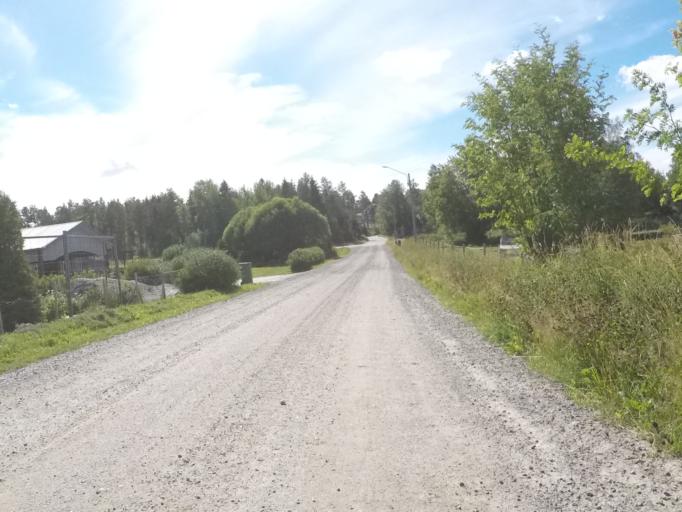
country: SE
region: Vaesterbotten
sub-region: Robertsfors Kommun
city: Robertsfors
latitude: 64.0000
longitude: 20.8112
